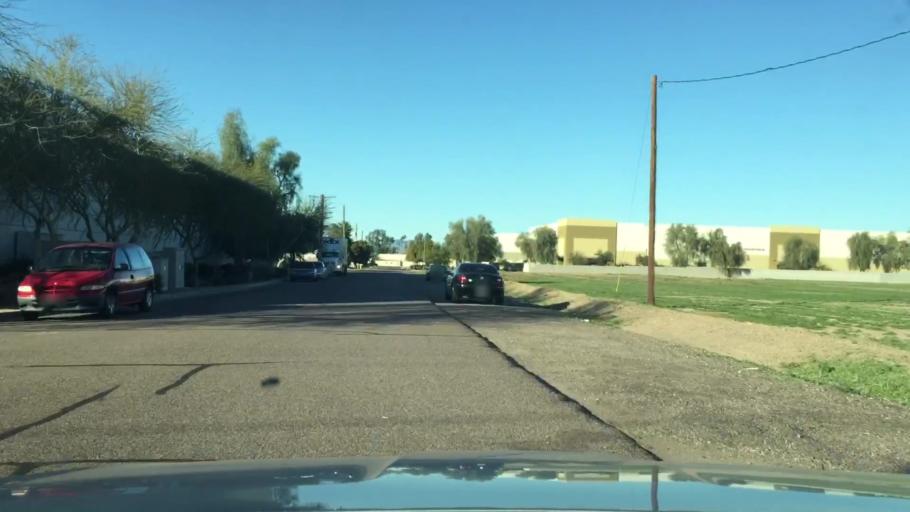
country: US
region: Arizona
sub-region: Maricopa County
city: Guadalupe
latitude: 33.3929
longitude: -111.9999
